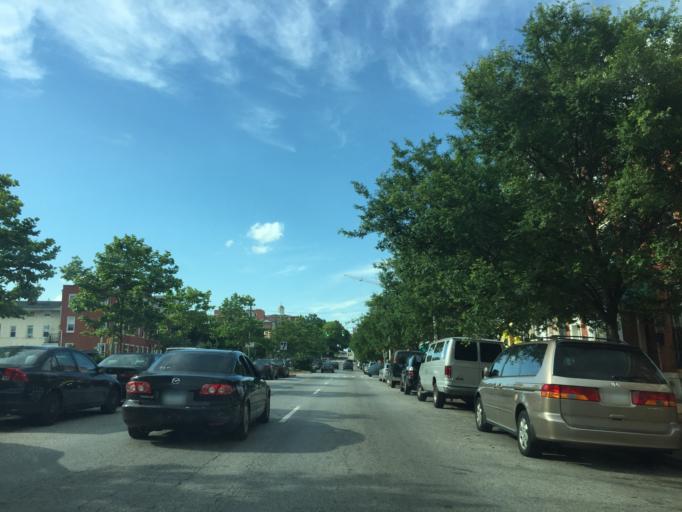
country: US
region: Maryland
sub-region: City of Baltimore
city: Baltimore
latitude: 39.2898
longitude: -76.5937
